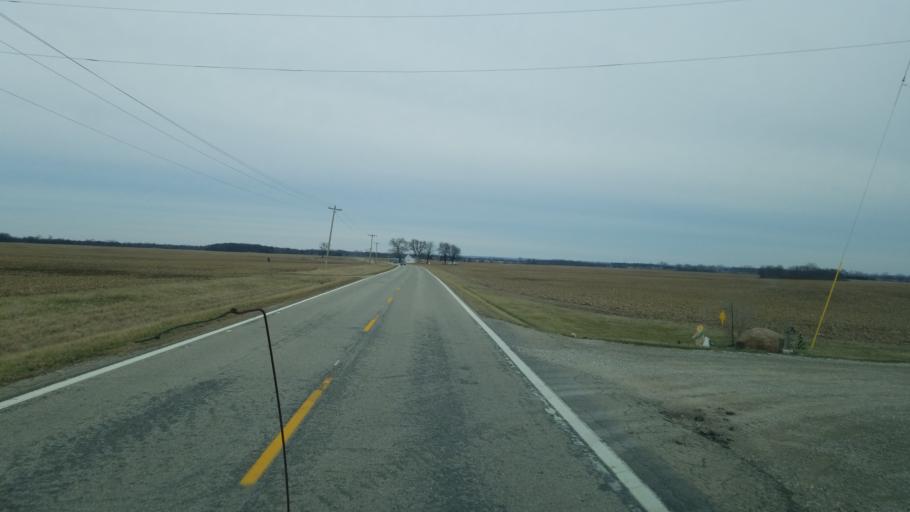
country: US
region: Ohio
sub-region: Pickaway County
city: Williamsport
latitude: 39.5575
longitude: -83.0941
